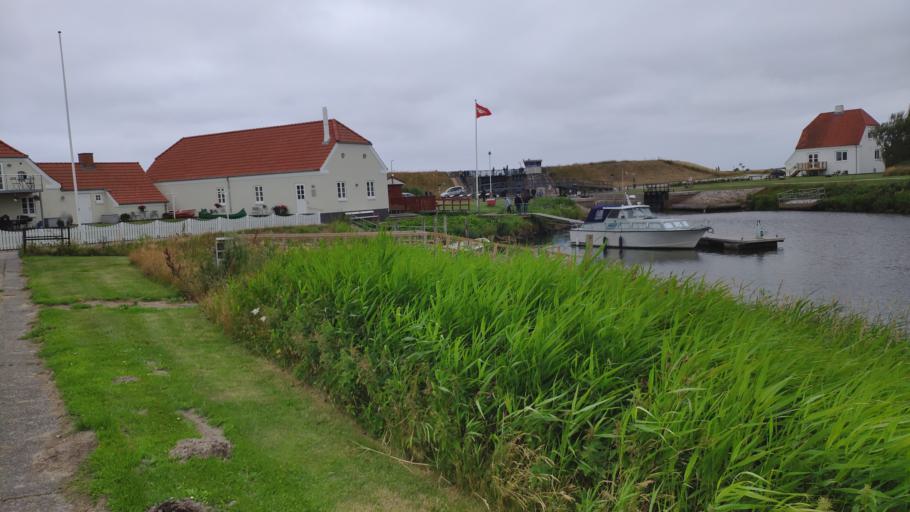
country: DK
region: South Denmark
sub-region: Esbjerg Kommune
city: Ribe
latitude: 55.3391
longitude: 8.6777
